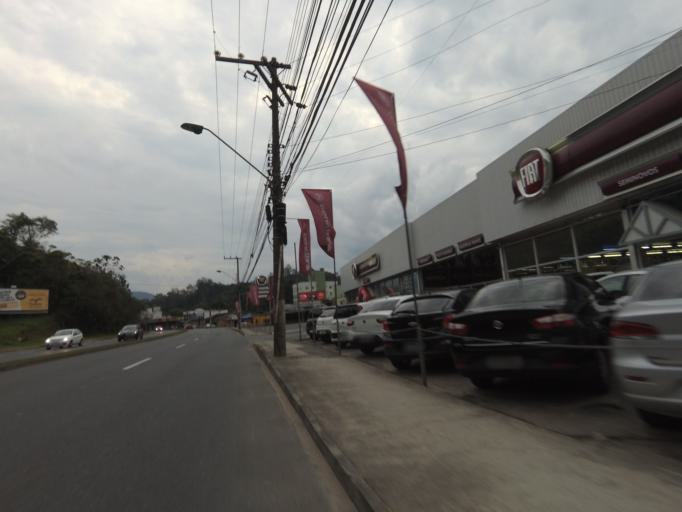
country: BR
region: Santa Catarina
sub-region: Blumenau
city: Blumenau
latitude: -26.9037
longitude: -49.0641
